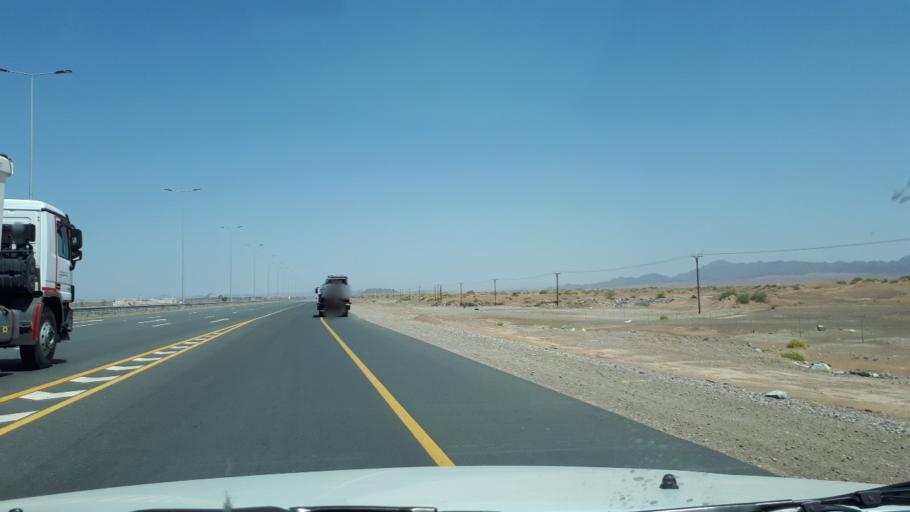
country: OM
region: Ash Sharqiyah
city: Al Qabil
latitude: 22.5265
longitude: 58.7391
